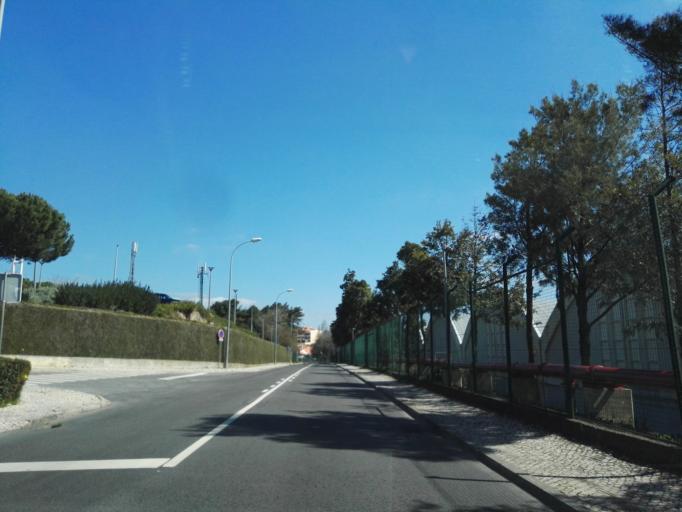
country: PT
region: Lisbon
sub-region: Sintra
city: Rio de Mouro
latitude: 38.7523
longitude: -9.3461
